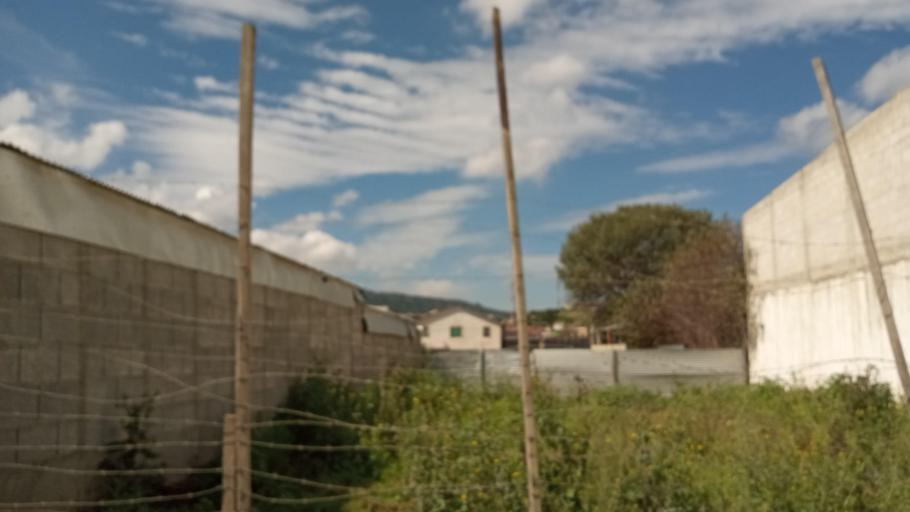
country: GT
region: Quetzaltenango
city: Quetzaltenango
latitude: 14.8458
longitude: -91.5084
